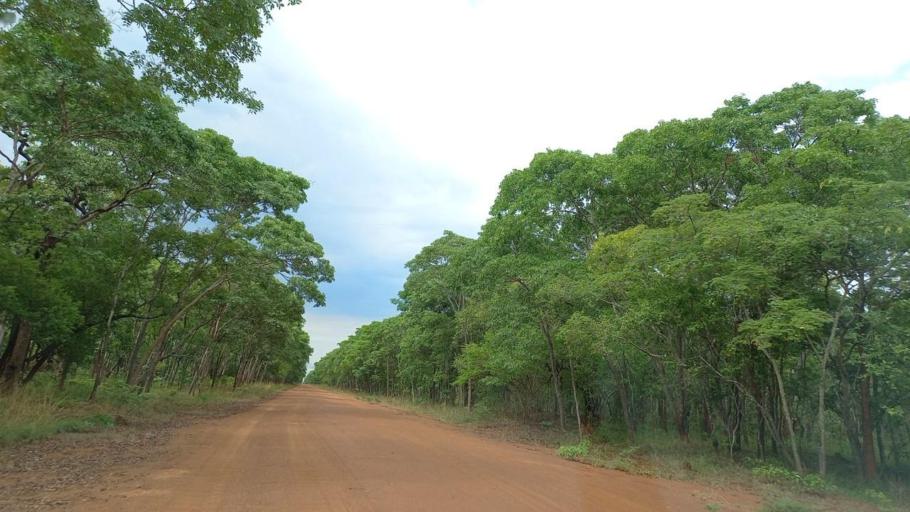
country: ZM
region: North-Western
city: Kalengwa
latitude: -13.4193
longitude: 25.0561
